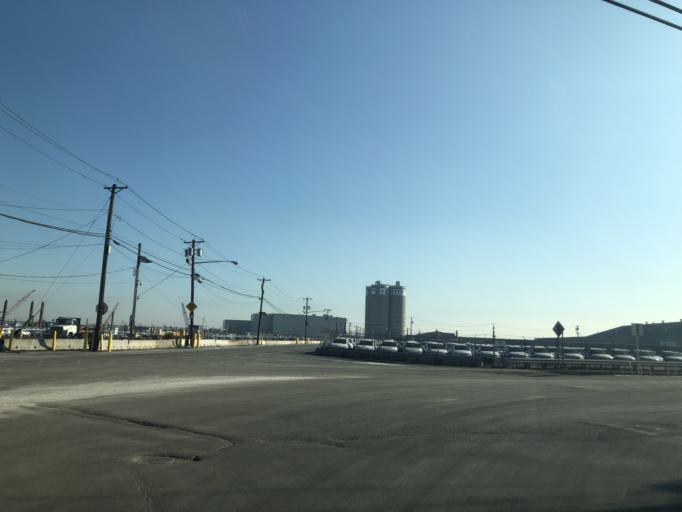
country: US
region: New Jersey
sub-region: Hudson County
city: Bayonne
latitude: 40.6922
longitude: -74.1425
